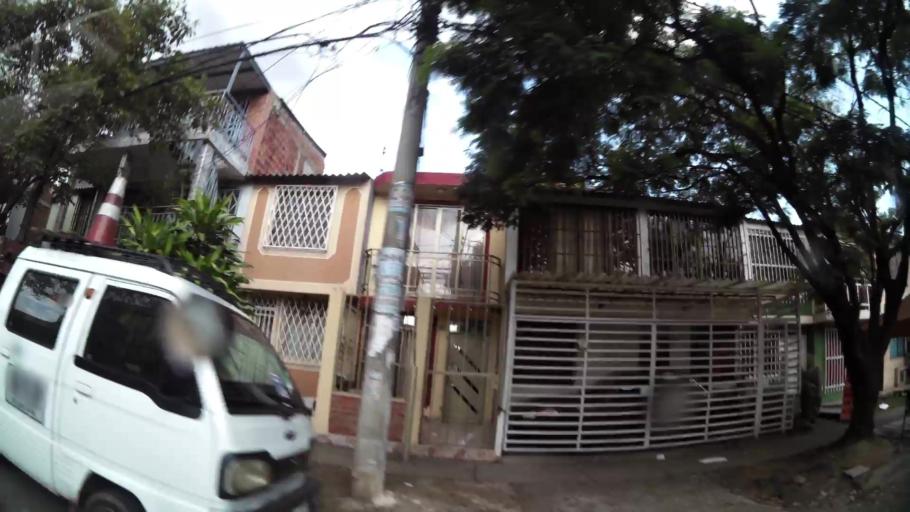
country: CO
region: Valle del Cauca
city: Cali
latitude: 3.4676
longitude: -76.4869
